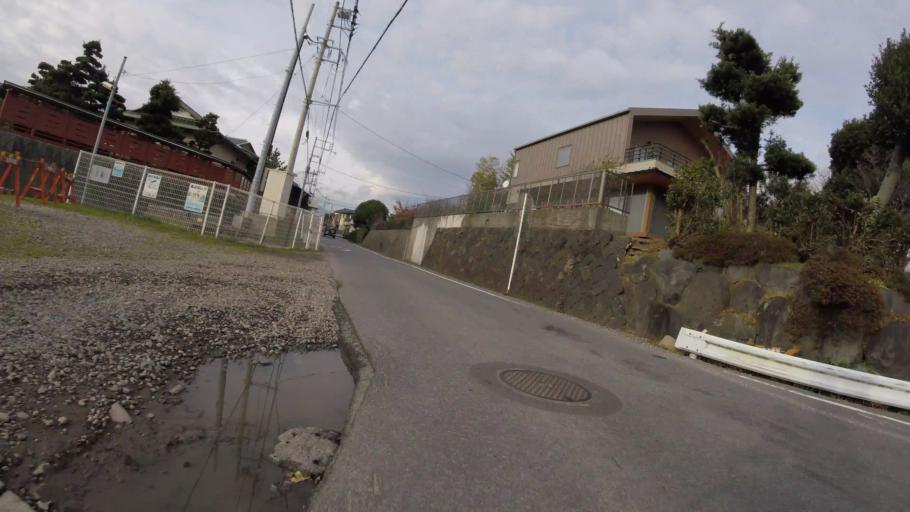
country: JP
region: Shizuoka
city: Mishima
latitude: 35.1048
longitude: 138.9122
